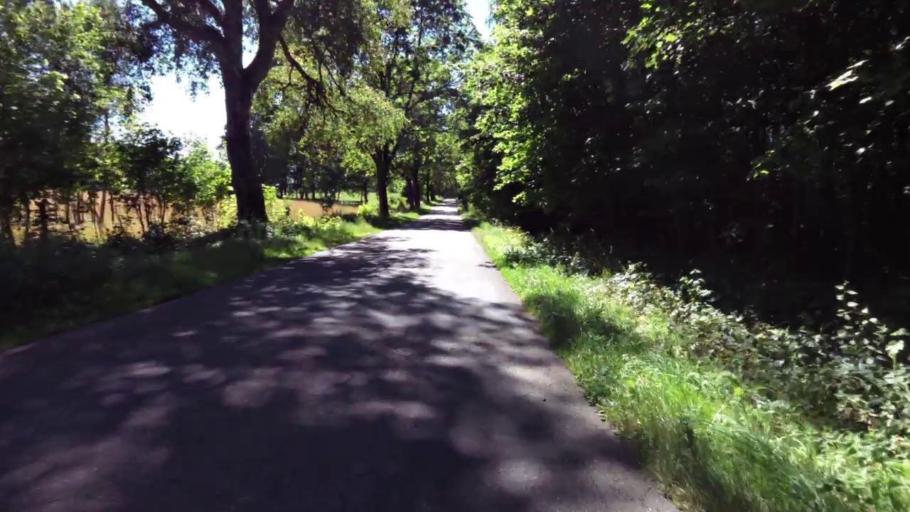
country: PL
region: West Pomeranian Voivodeship
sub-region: Powiat szczecinecki
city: Bialy Bor
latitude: 53.9736
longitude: 16.8660
